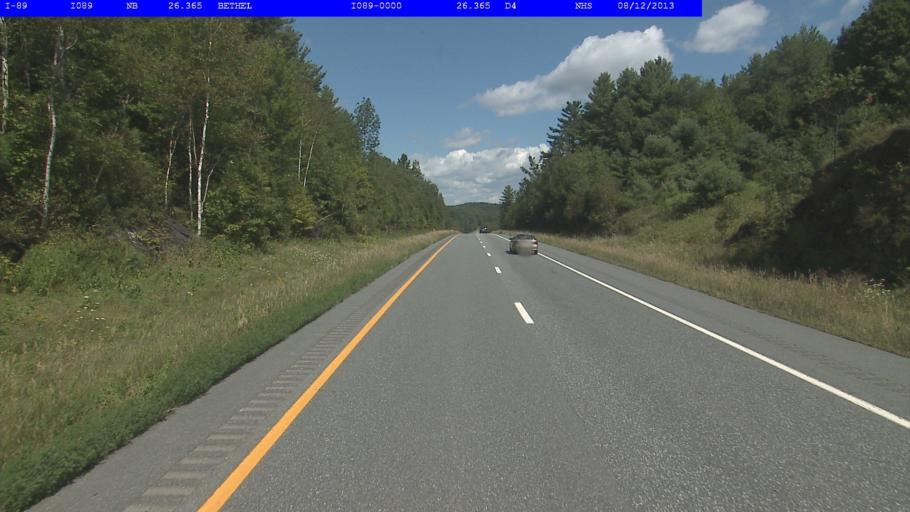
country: US
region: Vermont
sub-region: Orange County
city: Randolph
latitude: 43.8801
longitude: -72.6152
